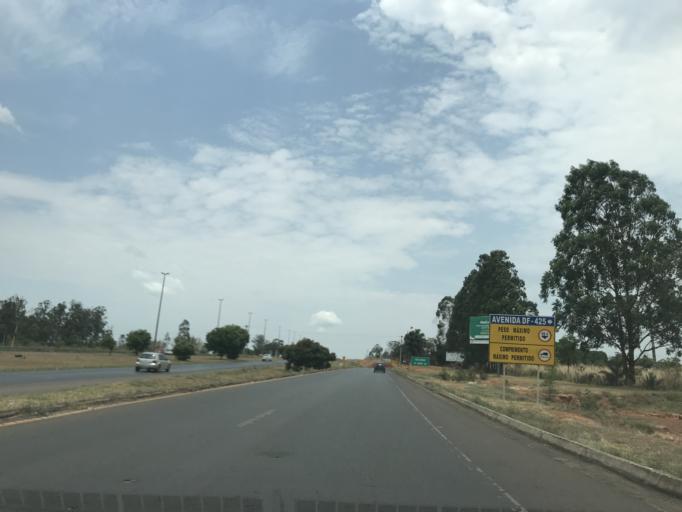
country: BR
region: Federal District
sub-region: Brasilia
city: Brasilia
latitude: -15.6689
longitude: -47.8144
